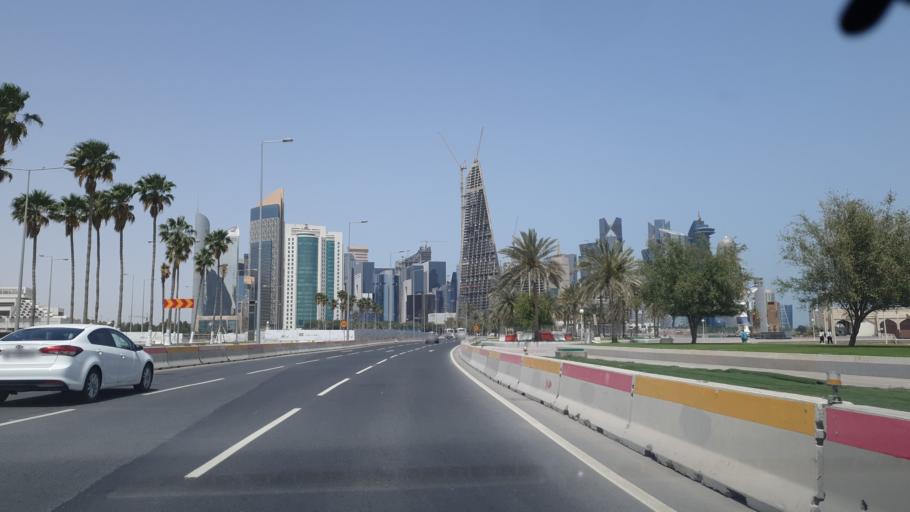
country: QA
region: Baladiyat ad Dawhah
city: Doha
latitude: 25.3063
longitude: 51.5182
